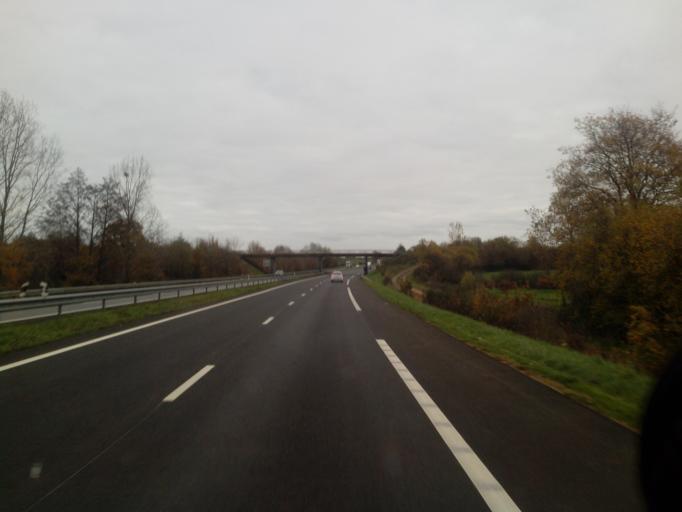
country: FR
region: Pays de la Loire
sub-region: Departement de Maine-et-Loire
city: Saint-Andre-de-la-Marche
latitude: 47.0881
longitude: -0.9832
